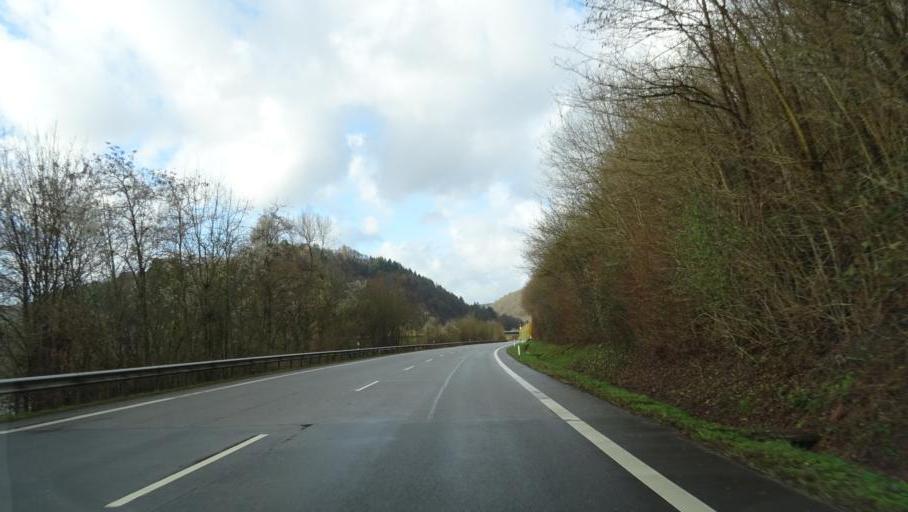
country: DE
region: Baden-Wuerttemberg
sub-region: Karlsruhe Region
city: Neckargerach
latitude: 49.3942
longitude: 9.0783
